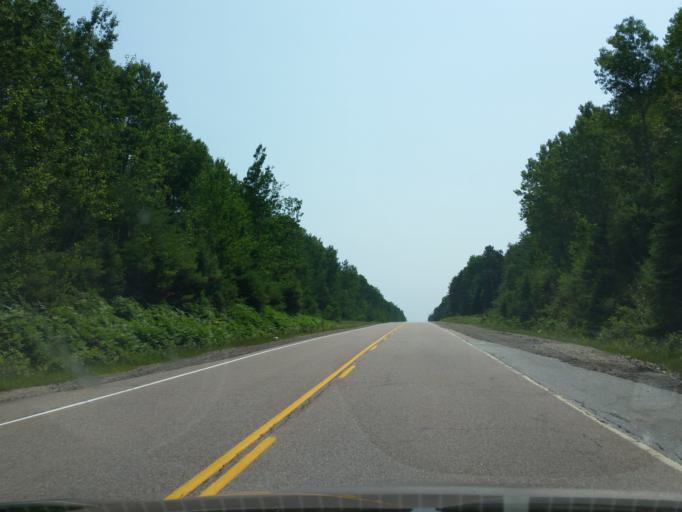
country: CA
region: Ontario
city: Deep River
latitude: 46.1883
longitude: -77.8717
